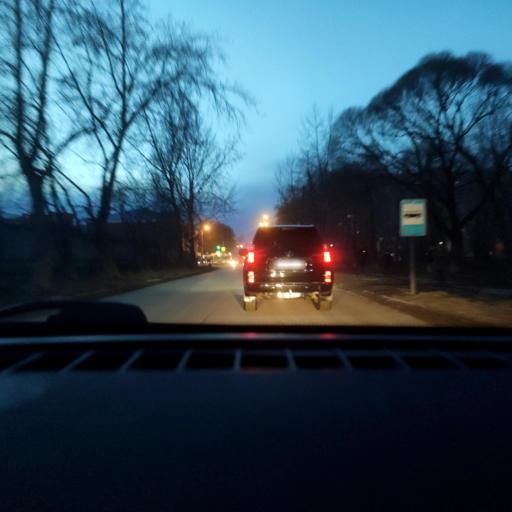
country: RU
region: Perm
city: Froly
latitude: 57.9665
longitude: 56.2669
